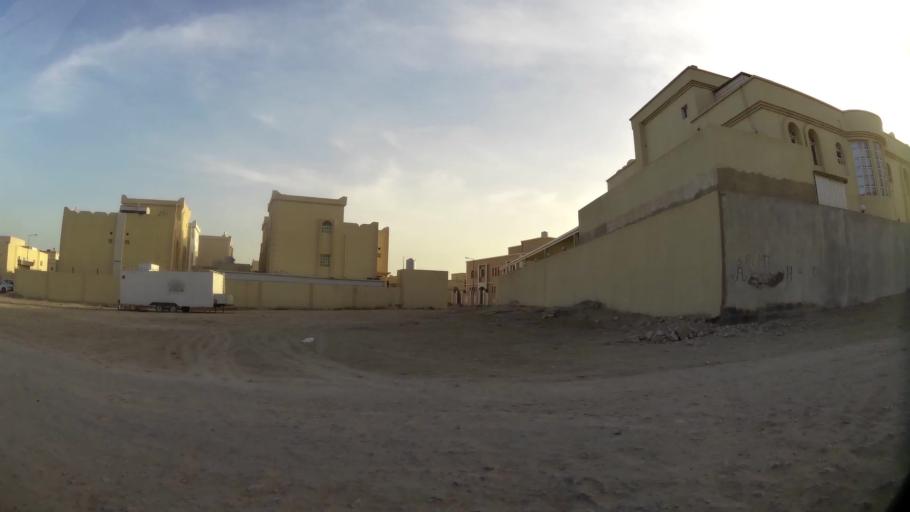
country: QA
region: Al Wakrah
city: Al Wakrah
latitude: 25.1471
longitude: 51.6110
